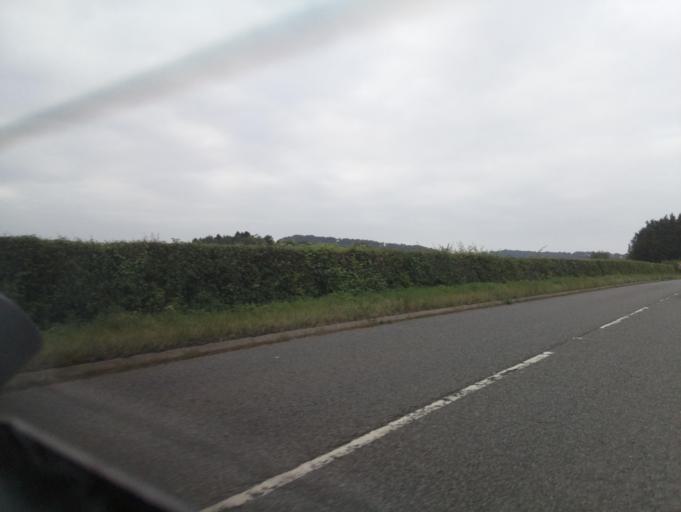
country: GB
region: England
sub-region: Shropshire
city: Shawbury
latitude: 52.8274
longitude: -2.6017
